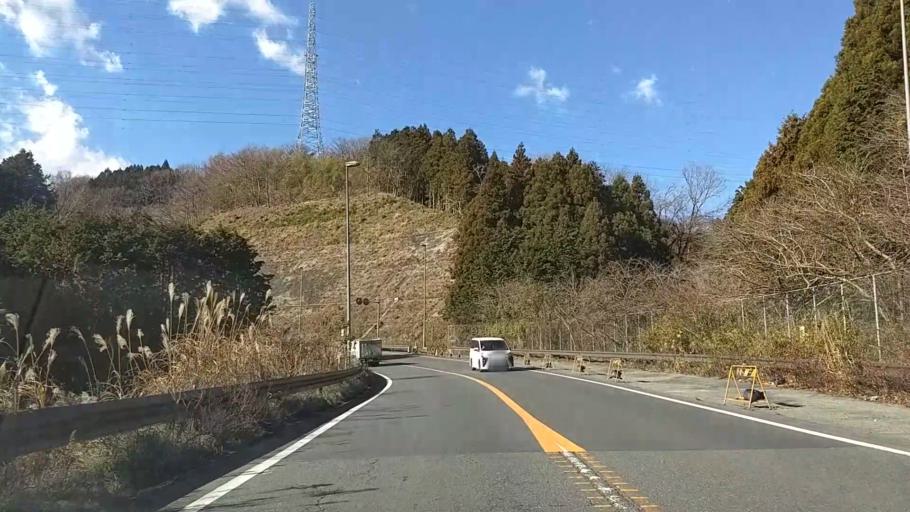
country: JP
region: Shizuoka
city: Gotemba
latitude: 35.3564
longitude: 138.9649
